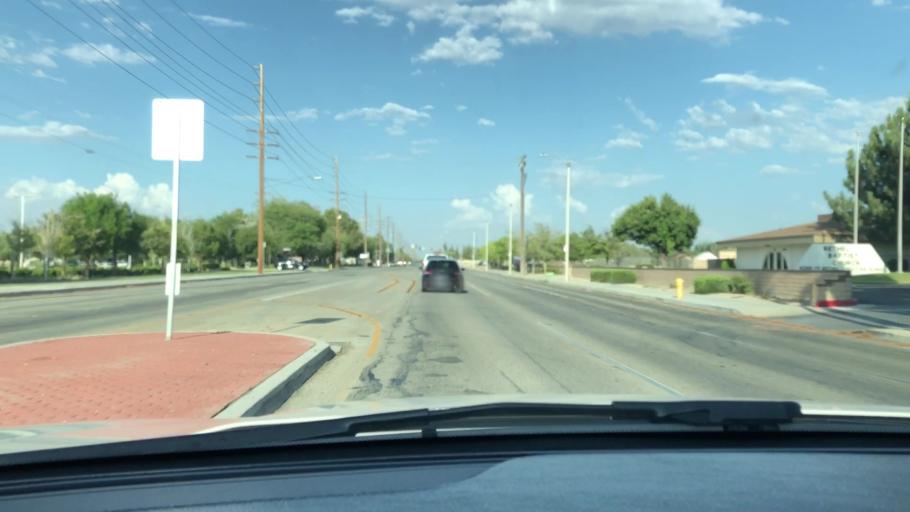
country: US
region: California
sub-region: Los Angeles County
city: Quartz Hill
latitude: 34.6748
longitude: -118.1869
